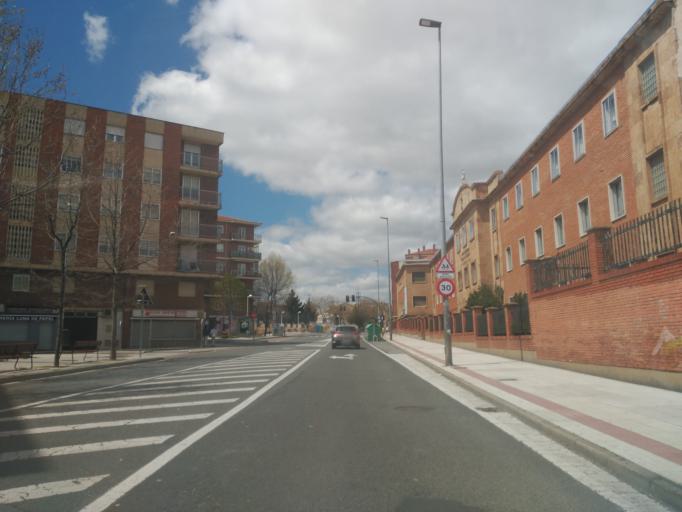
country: ES
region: Castille and Leon
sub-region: Provincia de Salamanca
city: Salamanca
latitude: 40.9742
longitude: -5.6717
